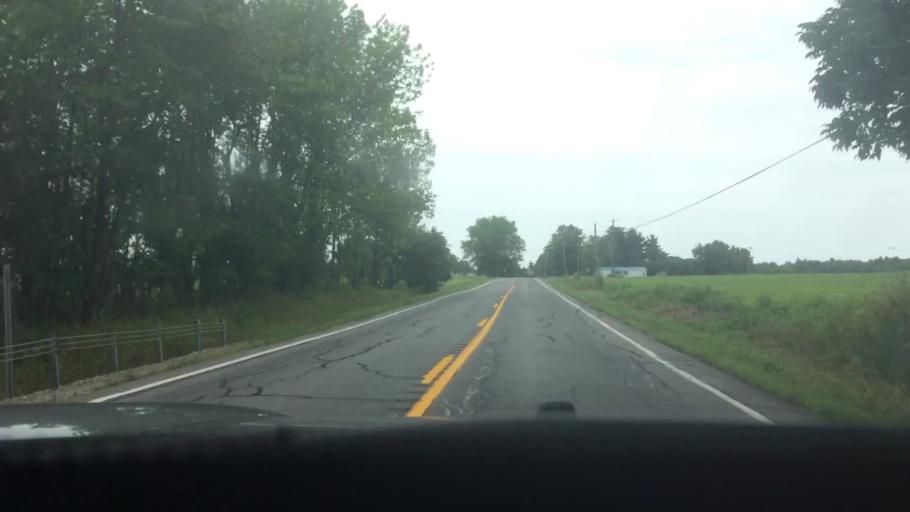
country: US
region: New York
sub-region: St. Lawrence County
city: Hannawa Falls
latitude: 44.6711
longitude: -74.7323
